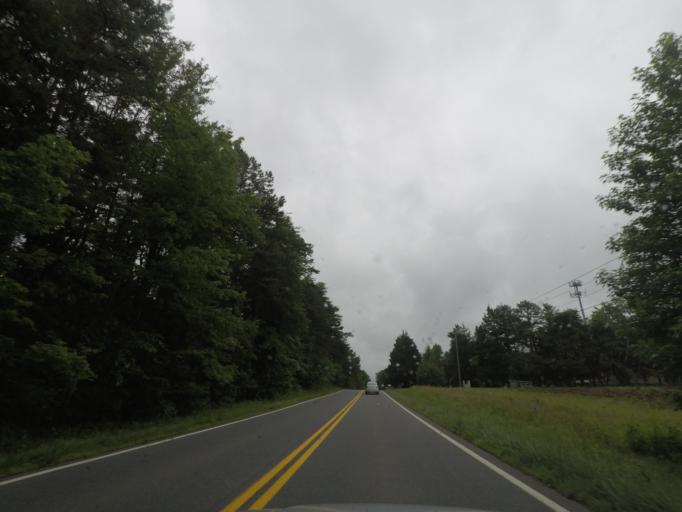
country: US
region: Virginia
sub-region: Fluvanna County
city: Palmyra
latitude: 37.9356
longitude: -78.2470
